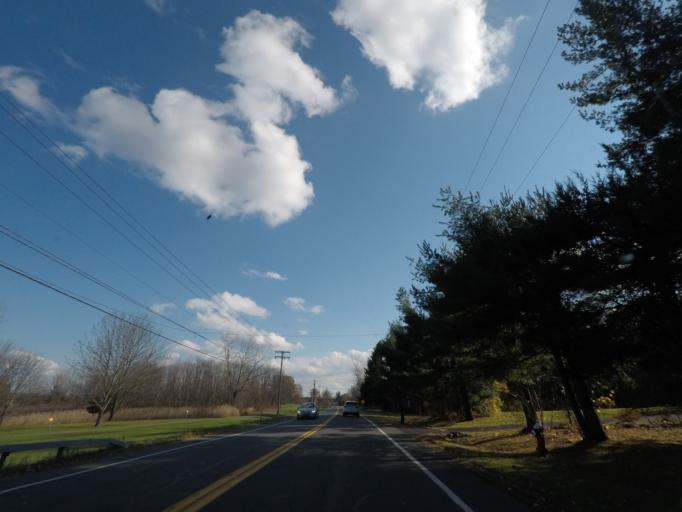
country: US
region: New York
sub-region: Schenectady County
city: Niskayuna
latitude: 42.8177
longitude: -73.8682
